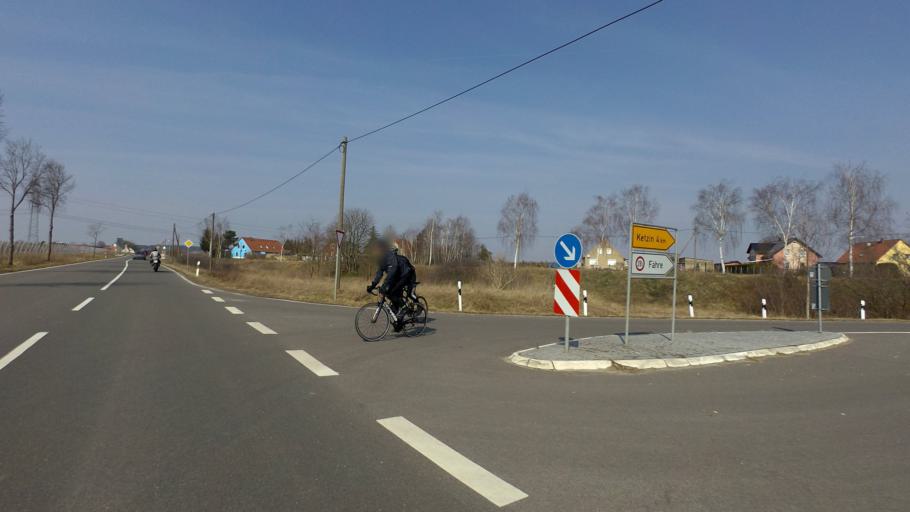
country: DE
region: Brandenburg
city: Ketzin
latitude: 52.4534
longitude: 12.8275
